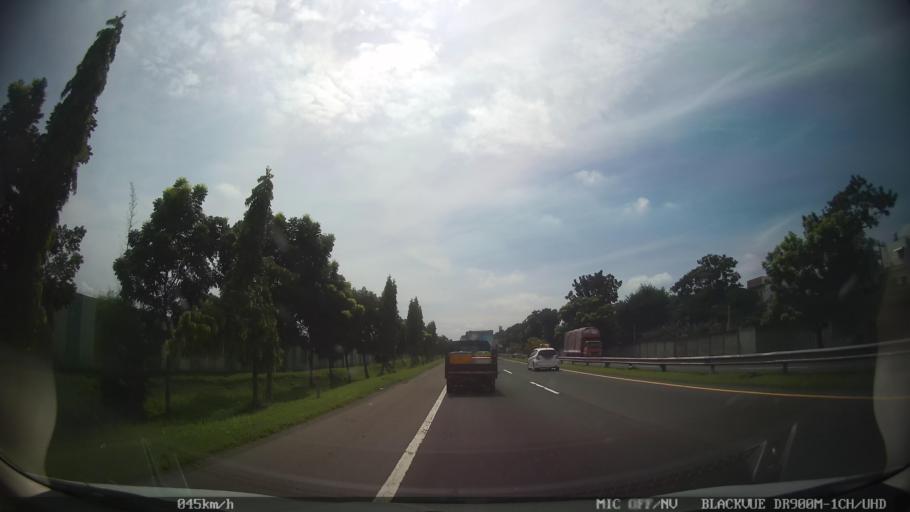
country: ID
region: North Sumatra
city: Medan
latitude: 3.6389
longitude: 98.7023
